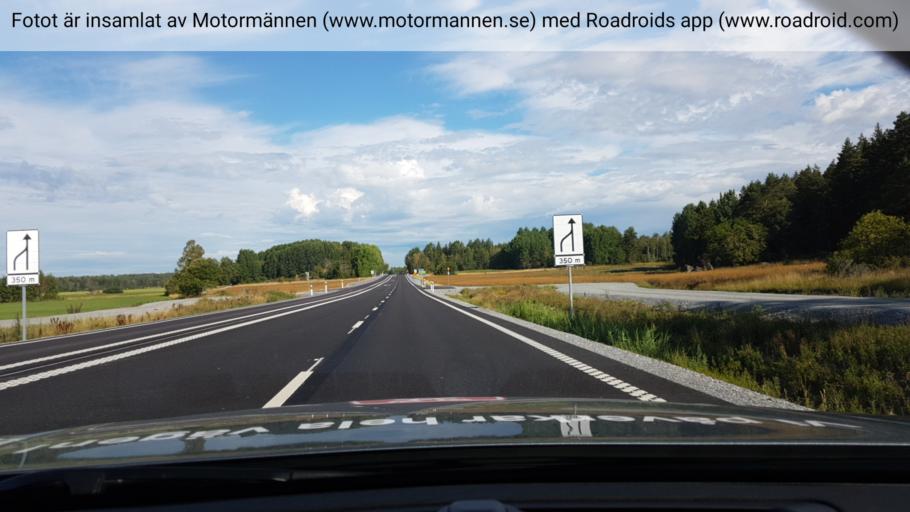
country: SE
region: Uppsala
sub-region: Enkopings Kommun
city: Irsta
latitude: 59.7060
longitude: 16.9868
